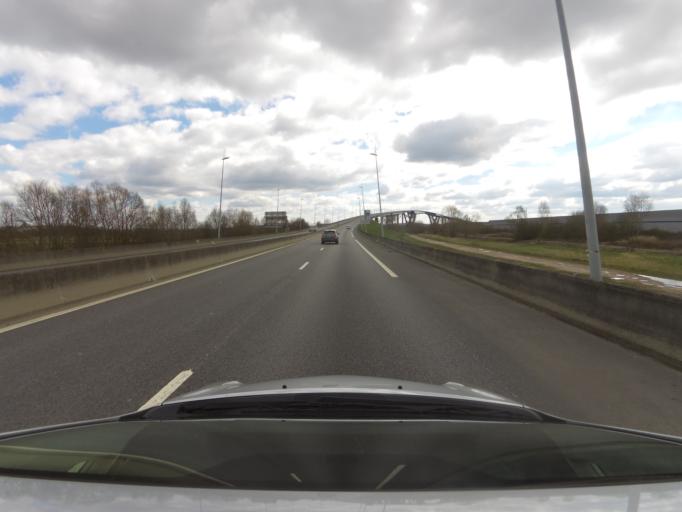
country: FR
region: Haute-Normandie
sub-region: Departement de la Seine-Maritime
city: Rogerville
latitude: 49.4741
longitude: 0.2695
